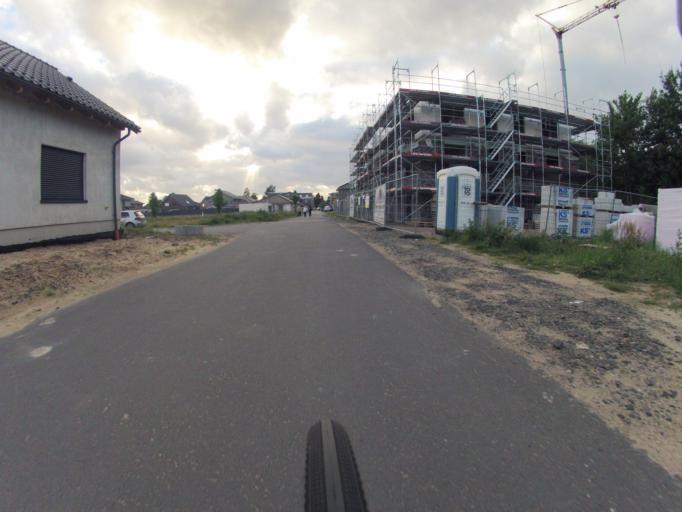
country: DE
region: North Rhine-Westphalia
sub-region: Regierungsbezirk Munster
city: Birgte
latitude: 52.2948
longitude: 7.6464
